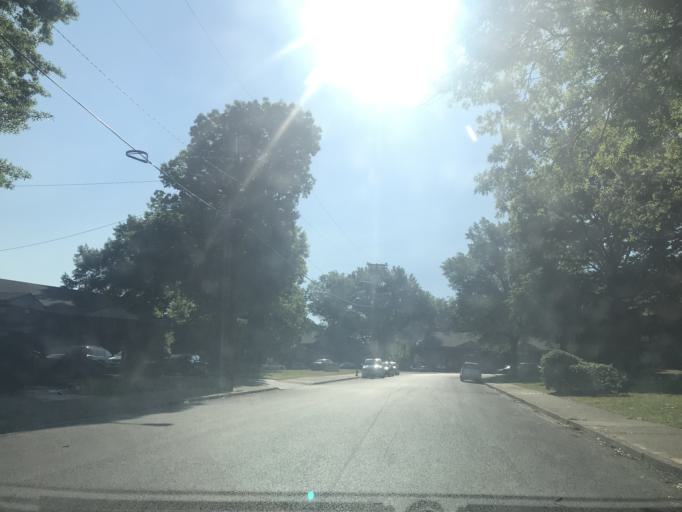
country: US
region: Tennessee
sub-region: Davidson County
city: Nashville
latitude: 36.1905
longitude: -86.8176
